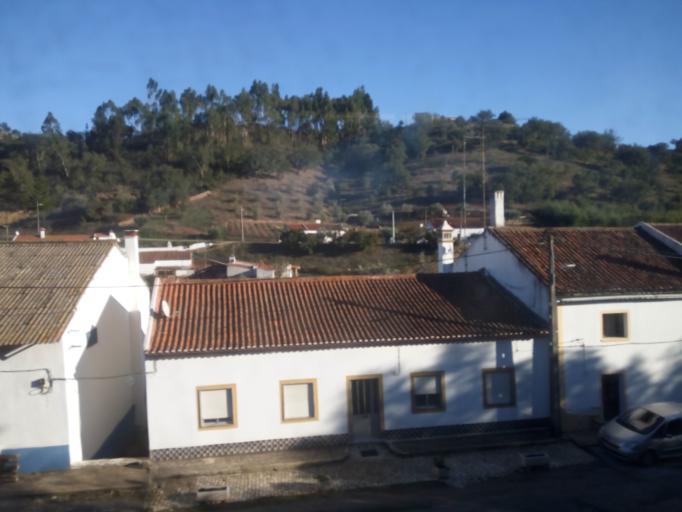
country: PT
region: Beja
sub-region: Odemira
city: Odemira
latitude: 37.5893
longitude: -8.4898
